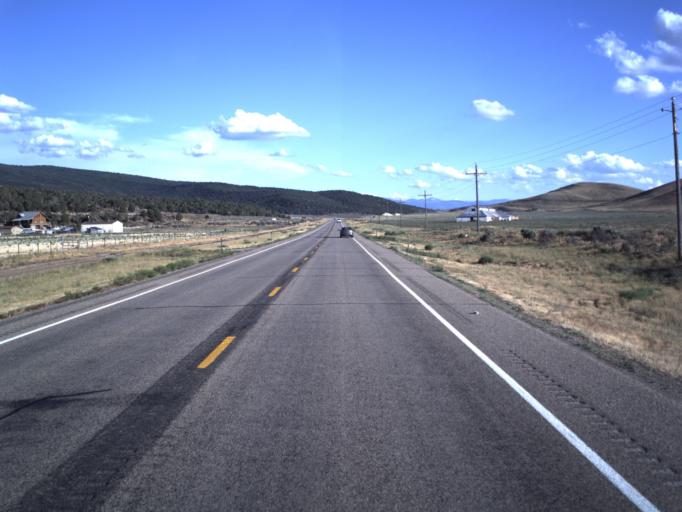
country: US
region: Utah
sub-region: Sanpete County
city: Fairview
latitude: 39.7727
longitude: -111.4884
